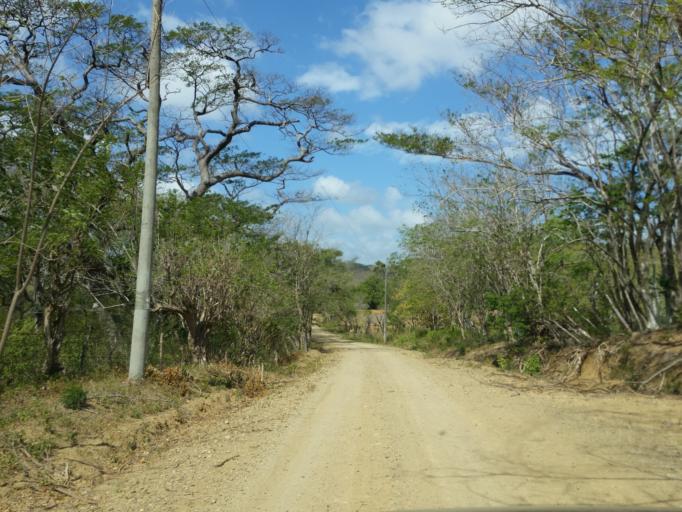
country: CR
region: Guanacaste
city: La Cruz
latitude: 11.1061
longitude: -85.7386
